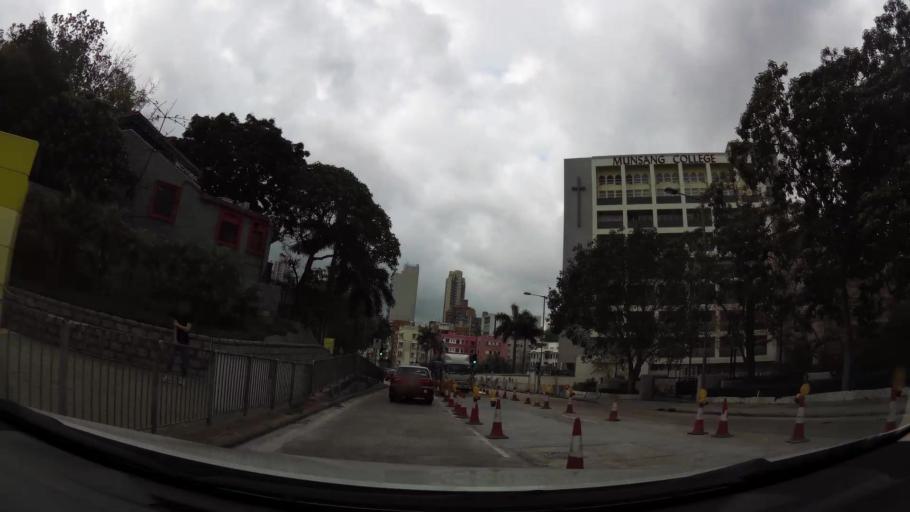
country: HK
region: Kowloon City
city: Kowloon
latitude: 22.3330
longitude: 114.1873
